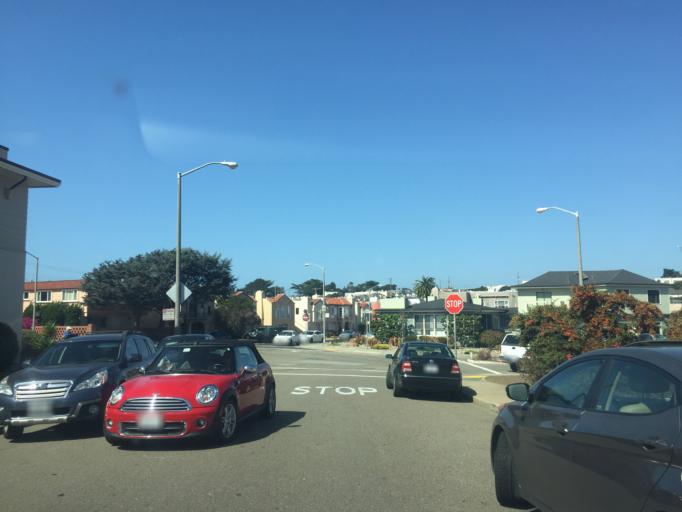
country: US
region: California
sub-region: San Mateo County
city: Daly City
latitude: 37.7370
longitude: -122.4910
